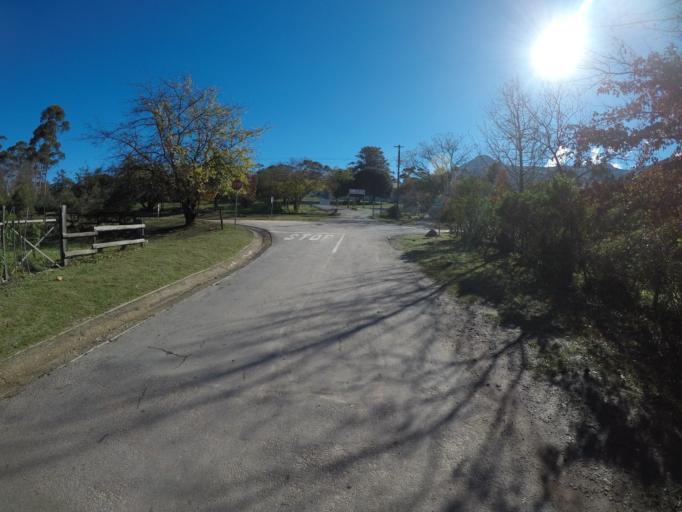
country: ZA
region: Western Cape
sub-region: Overberg District Municipality
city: Caledon
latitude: -34.0487
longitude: 19.6073
